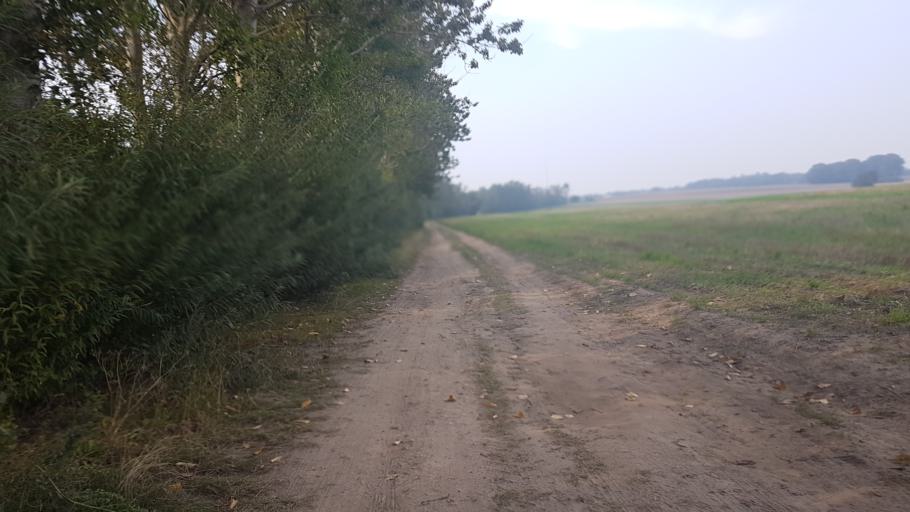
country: DE
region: Mecklenburg-Vorpommern
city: Garz
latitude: 54.2996
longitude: 13.3619
